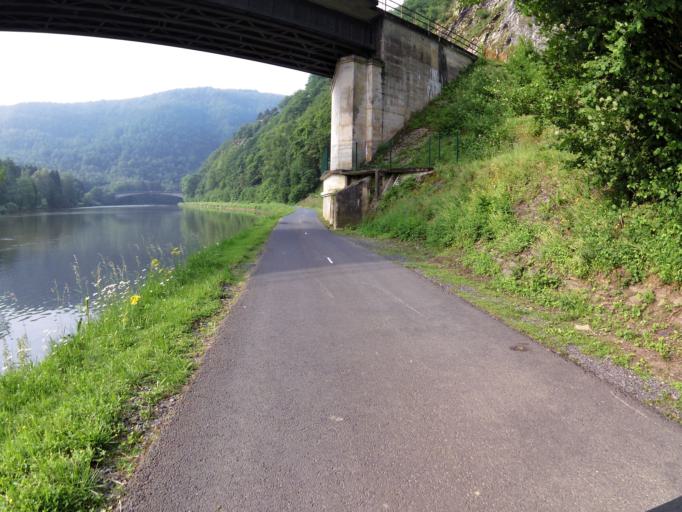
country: FR
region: Champagne-Ardenne
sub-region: Departement des Ardennes
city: Deville
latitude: 49.9098
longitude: 4.6880
